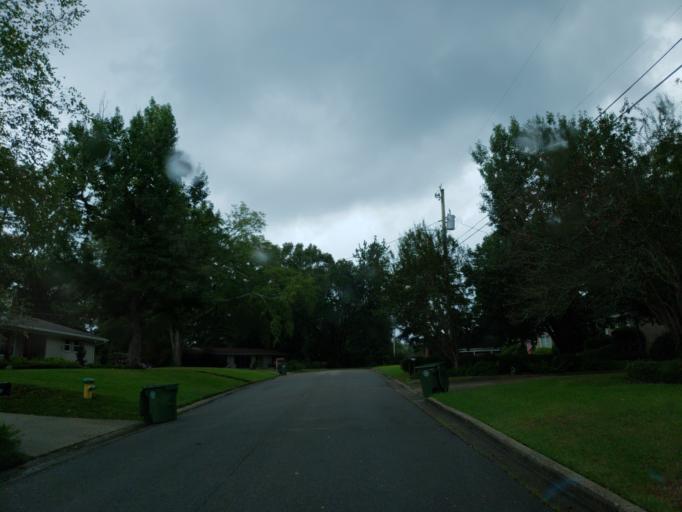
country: US
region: Mississippi
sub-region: Lamar County
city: West Hattiesburg
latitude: 31.3149
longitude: -89.3339
